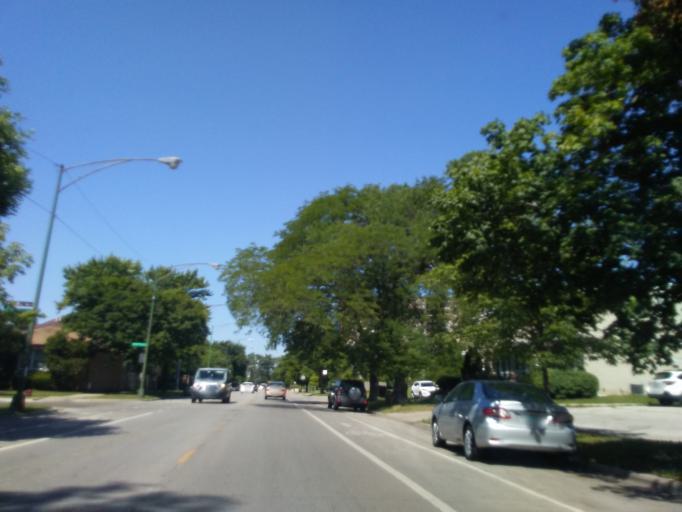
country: US
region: Illinois
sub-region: Cook County
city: Lincolnwood
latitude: 42.0048
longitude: -87.7055
